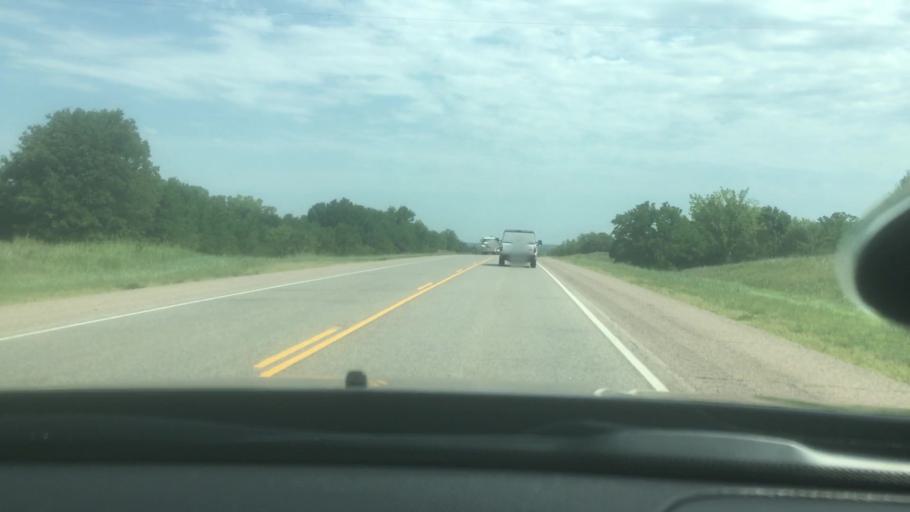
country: US
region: Oklahoma
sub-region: Seminole County
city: Maud
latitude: 35.0554
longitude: -96.9317
